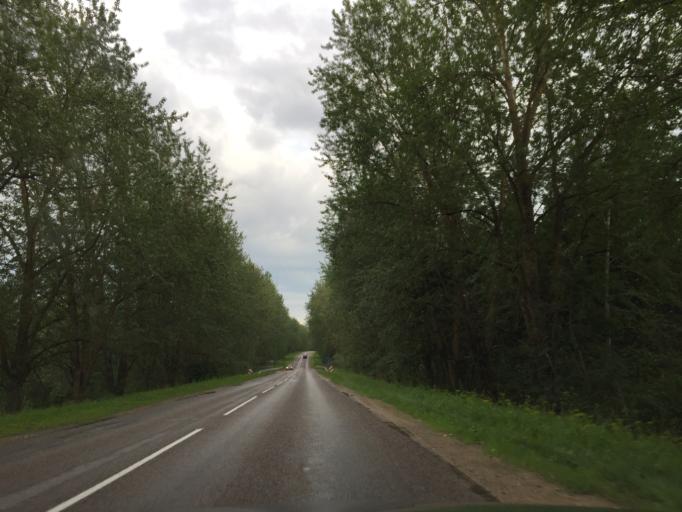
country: LV
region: Dobeles Rajons
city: Dobele
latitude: 56.5849
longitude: 23.2922
